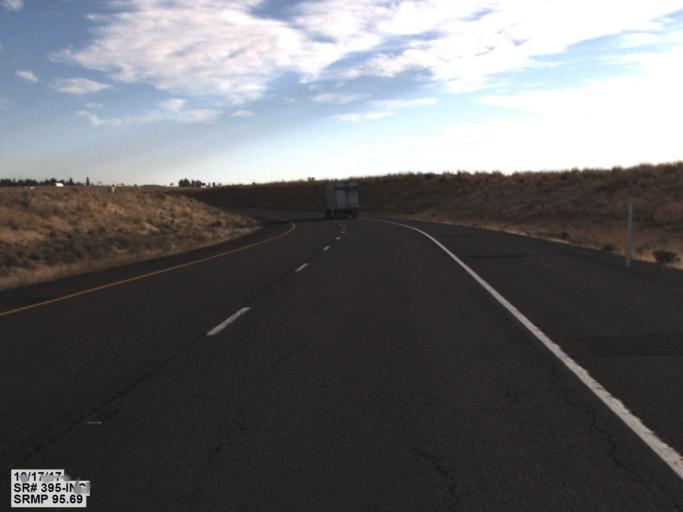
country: US
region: Washington
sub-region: Adams County
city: Ritzville
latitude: 47.1076
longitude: -118.3960
